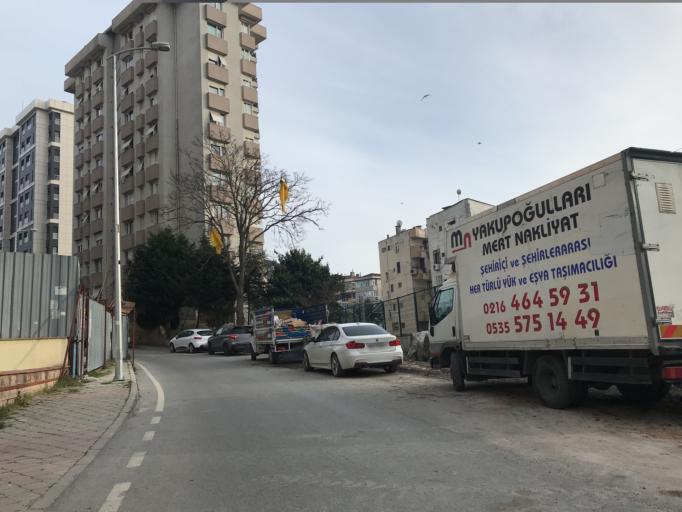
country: TR
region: Istanbul
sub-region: Atasehir
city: Atasehir
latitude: 40.9563
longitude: 29.0911
